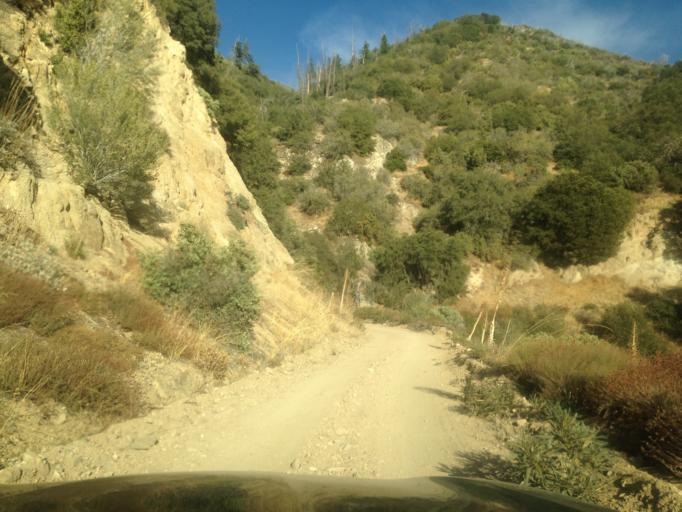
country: US
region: California
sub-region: San Bernardino County
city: Yucaipa
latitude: 34.1234
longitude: -117.0128
